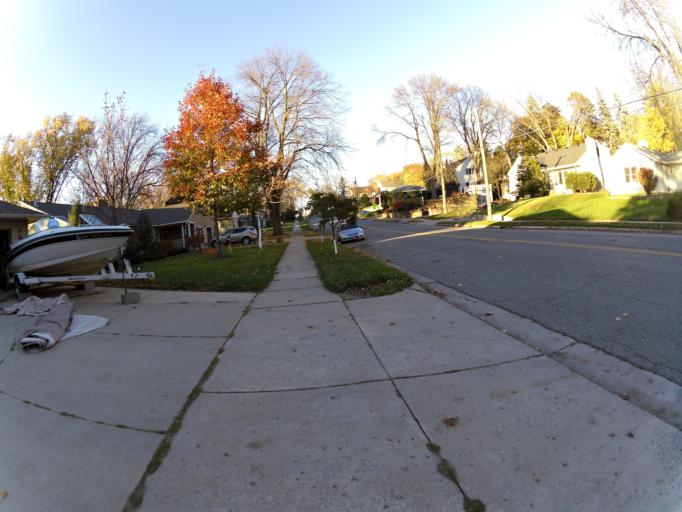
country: US
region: Minnesota
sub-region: Olmsted County
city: Rochester
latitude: 44.0146
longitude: -92.4841
